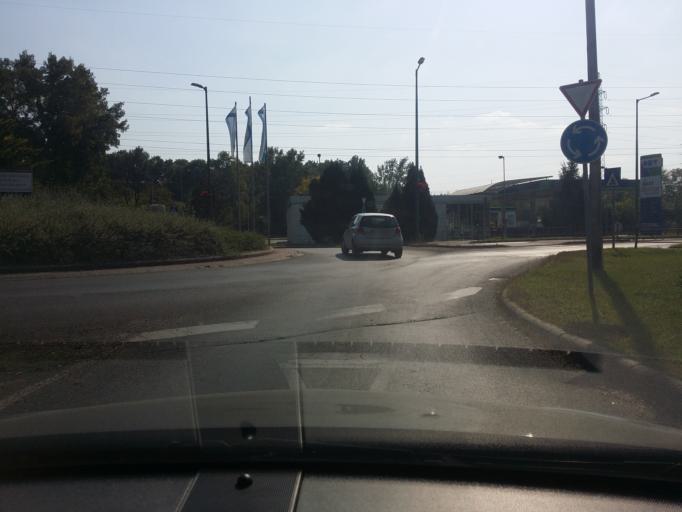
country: HU
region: Fejer
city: dunaujvaros
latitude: 46.9587
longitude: 18.9201
